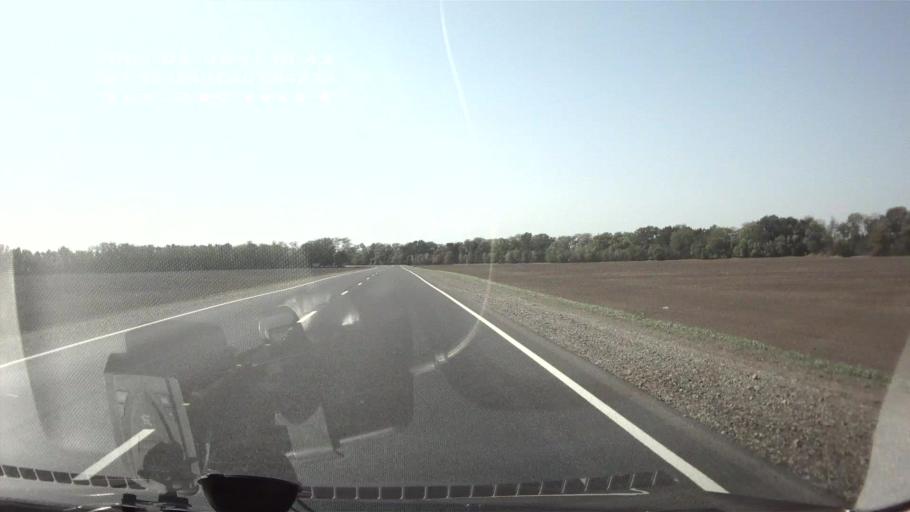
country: RU
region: Krasnodarskiy
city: Kavkazskaya
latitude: 45.5427
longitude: 40.6840
